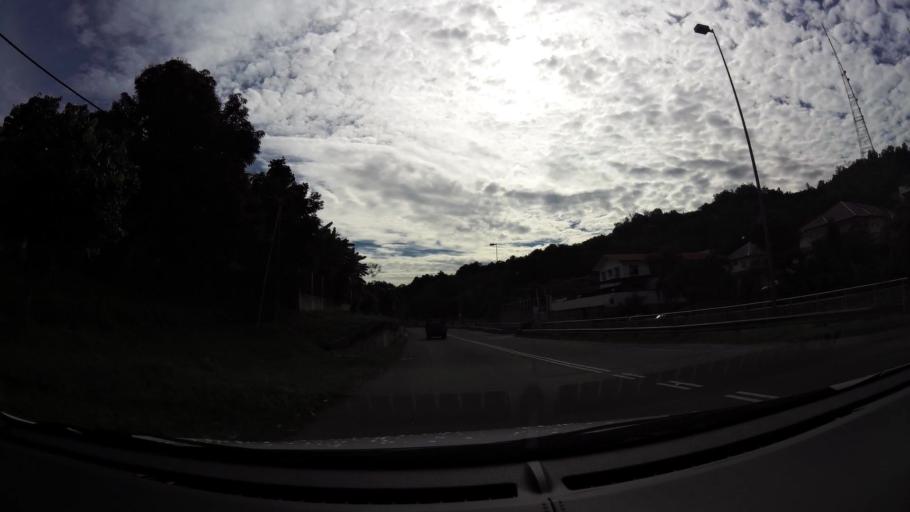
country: BN
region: Brunei and Muara
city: Bandar Seri Begawan
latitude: 4.8865
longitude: 114.9590
